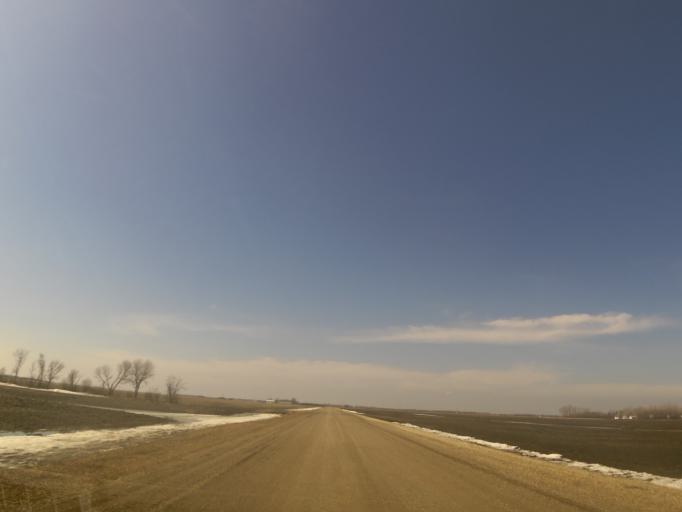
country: US
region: North Dakota
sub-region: Walsh County
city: Grafton
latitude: 48.4265
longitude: -97.2431
